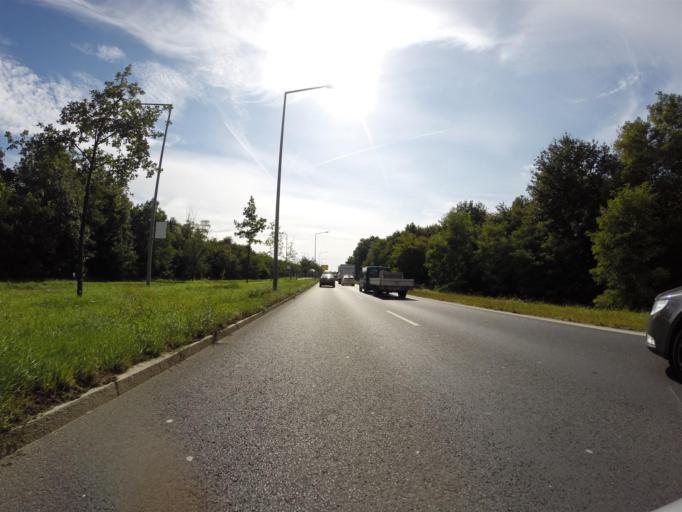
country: DE
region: Saxony
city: Albertstadt
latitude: 51.0979
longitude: 13.7361
